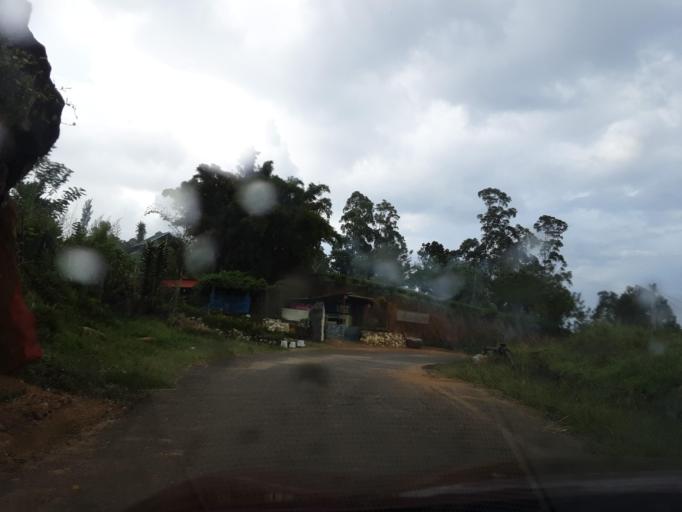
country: LK
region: Uva
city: Haputale
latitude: 6.8177
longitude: 80.8845
